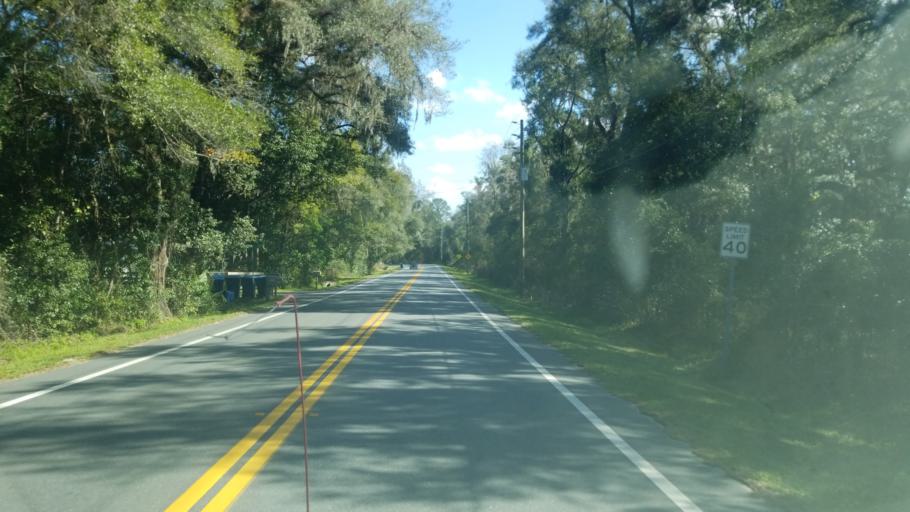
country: US
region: Florida
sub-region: Hernando County
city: North Brooksville
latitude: 28.6295
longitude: -82.3765
